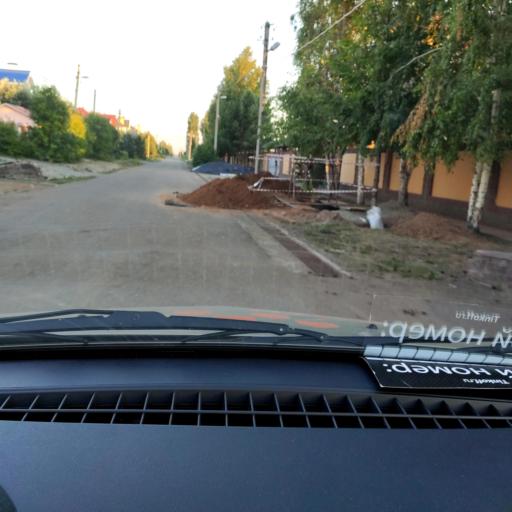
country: RU
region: Bashkortostan
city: Ufa
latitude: 54.6003
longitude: 55.9325
